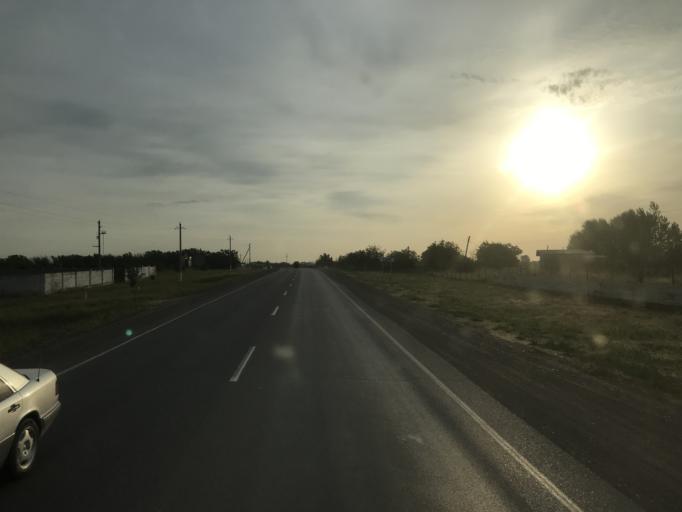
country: KZ
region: Ongtustik Qazaqstan
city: Saryaghash
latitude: 41.4353
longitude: 69.1162
